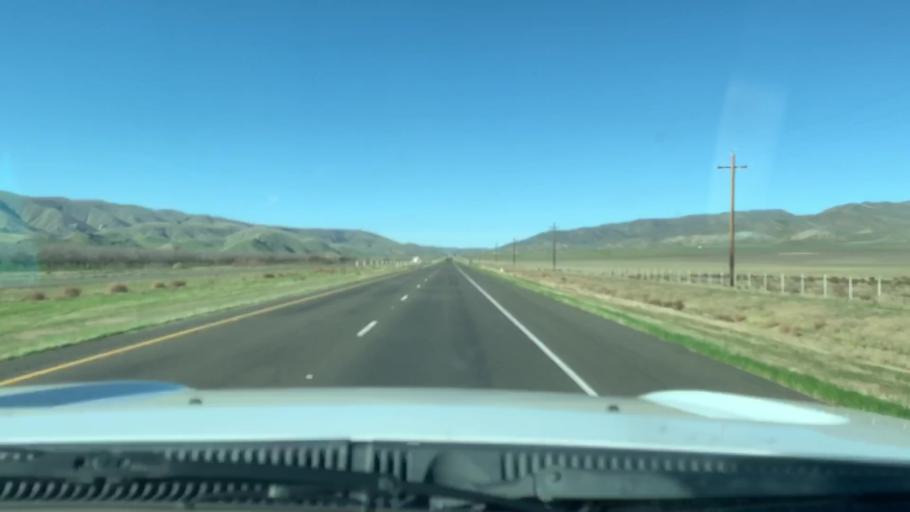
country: US
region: California
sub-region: San Luis Obispo County
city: Shandon
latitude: 35.6850
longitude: -120.1109
